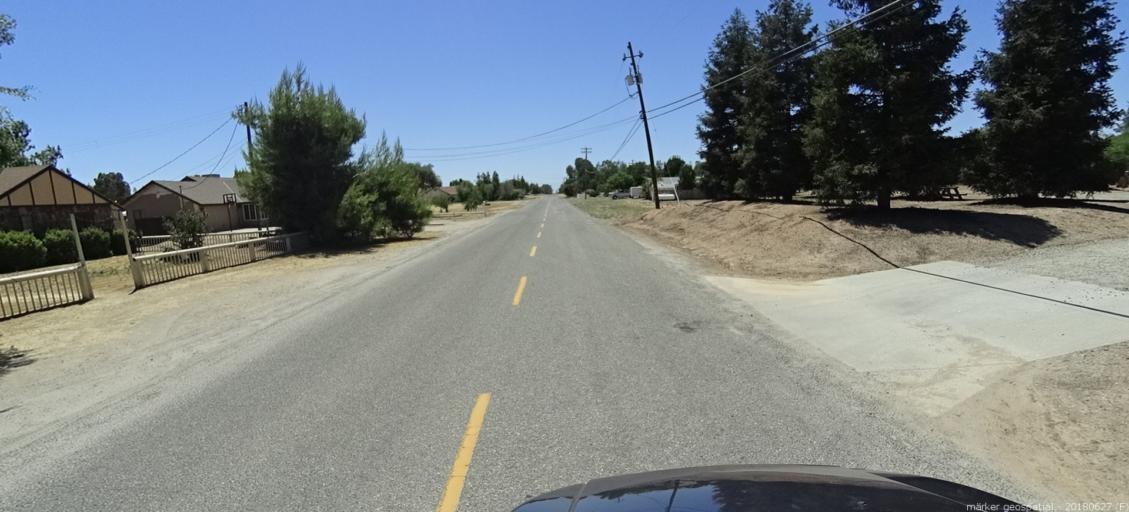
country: US
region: California
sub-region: Madera County
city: Bonadelle Ranchos-Madera Ranchos
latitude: 36.9642
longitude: -119.9013
